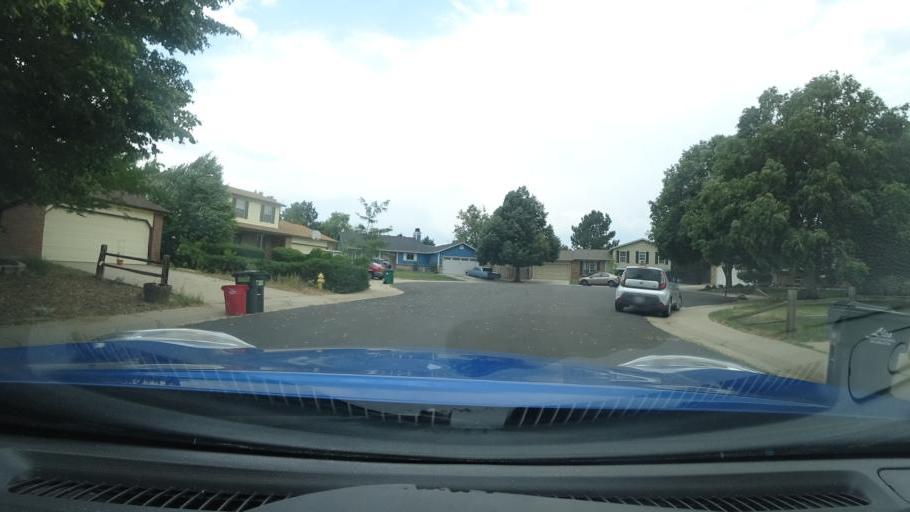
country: US
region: Colorado
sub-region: Adams County
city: Aurora
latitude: 39.6879
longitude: -104.7605
